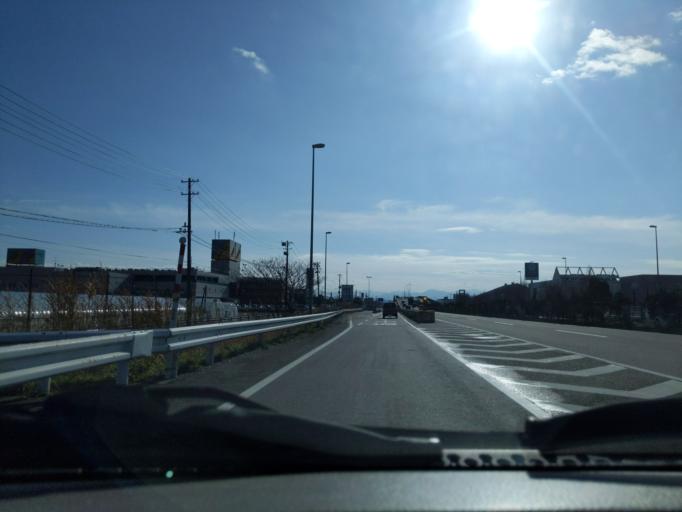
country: JP
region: Niigata
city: Kameda-honcho
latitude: 37.8736
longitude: 139.0858
